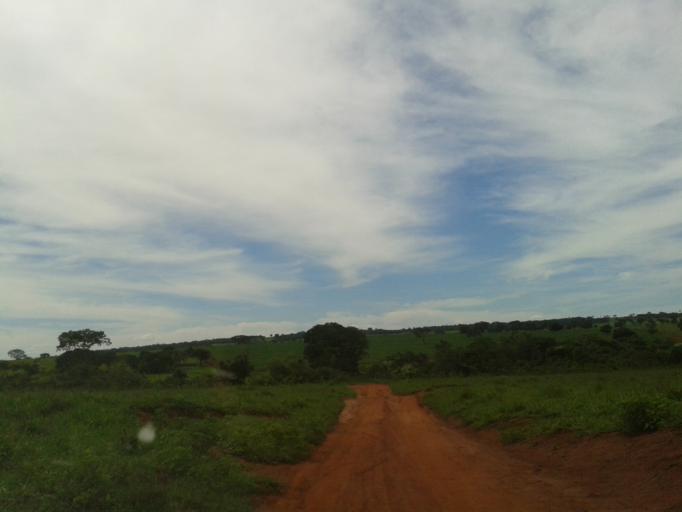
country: BR
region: Minas Gerais
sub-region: Capinopolis
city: Capinopolis
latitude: -18.7906
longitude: -49.8013
